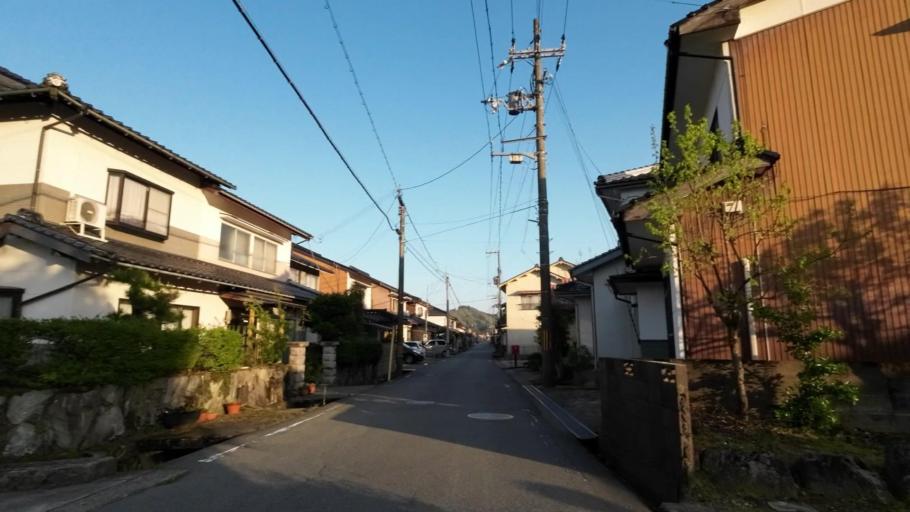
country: JP
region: Hyogo
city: Toyooka
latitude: 35.3687
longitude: 134.8142
